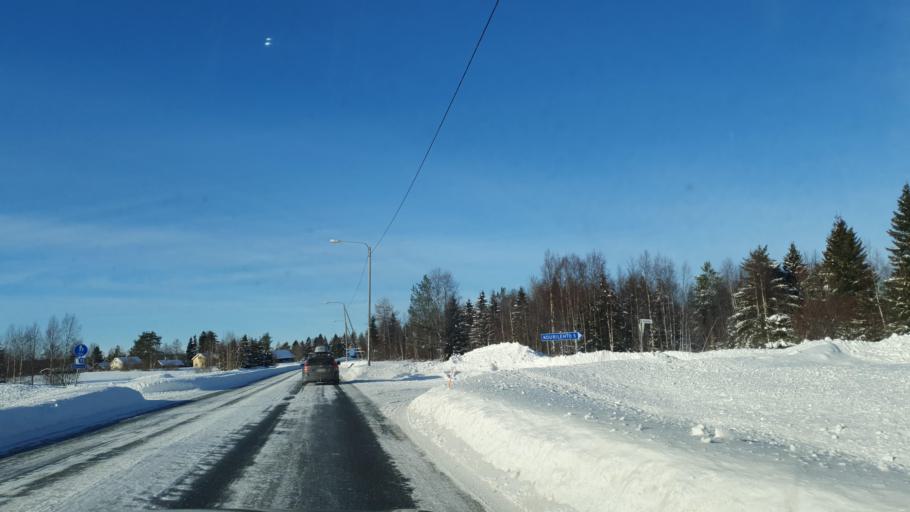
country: FI
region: Lapland
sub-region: Kemi-Tornio
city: Tornio
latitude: 65.9403
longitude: 24.0925
